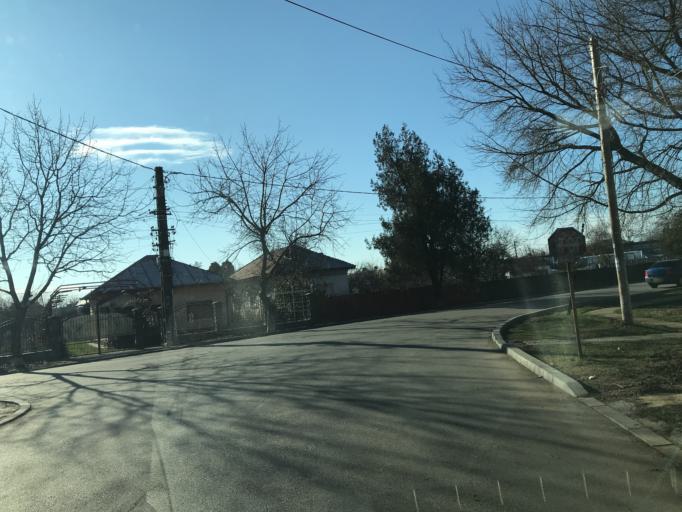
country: RO
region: Olt
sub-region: Comuna Piatra Olt
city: Piatra Olt
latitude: 44.3677
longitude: 24.2585
